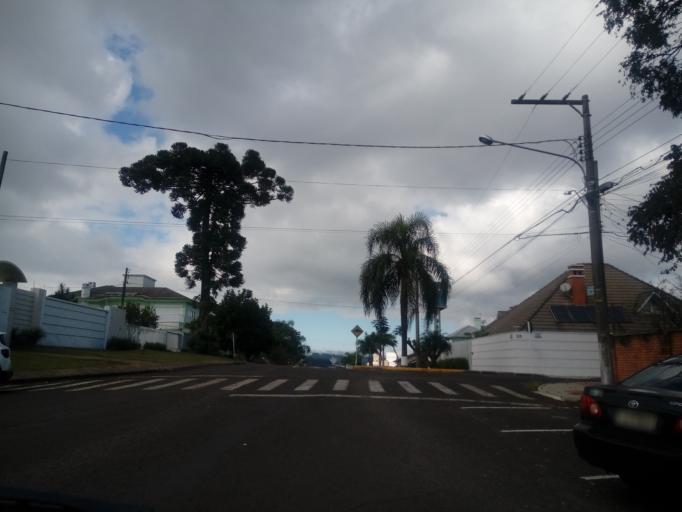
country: BR
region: Santa Catarina
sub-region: Chapeco
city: Chapeco
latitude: -27.1086
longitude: -52.6212
